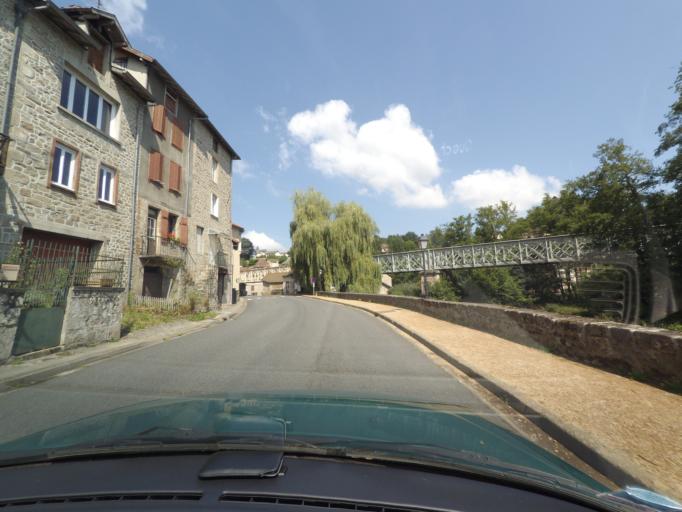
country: FR
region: Limousin
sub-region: Departement de la Haute-Vienne
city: Eymoutiers
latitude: 45.7393
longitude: 1.7450
